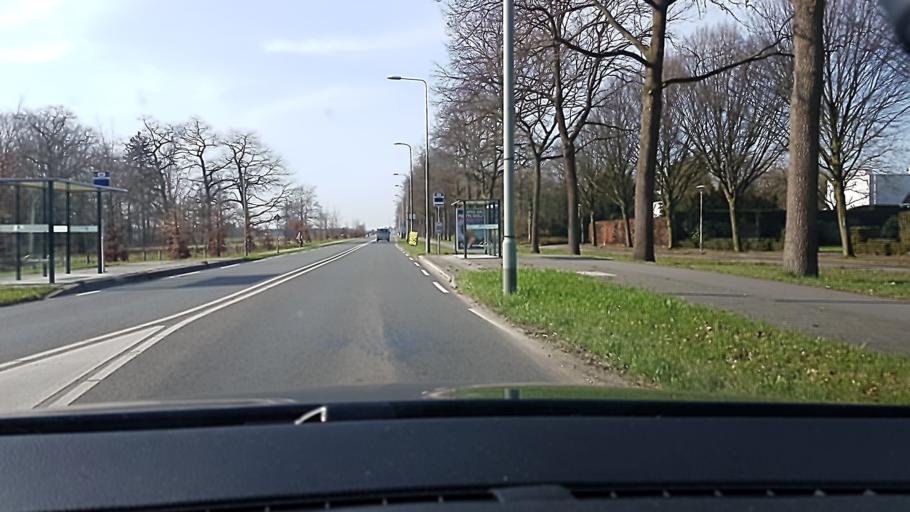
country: NL
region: Limburg
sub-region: Gemeente Roermond
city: Roermond
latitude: 51.1818
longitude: 5.9855
